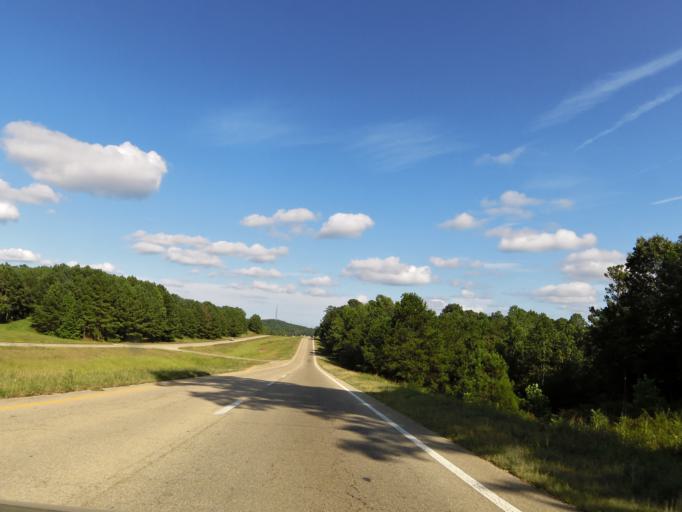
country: US
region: Mississippi
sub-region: Alcorn County
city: Farmington
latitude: 34.8538
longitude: -88.3624
